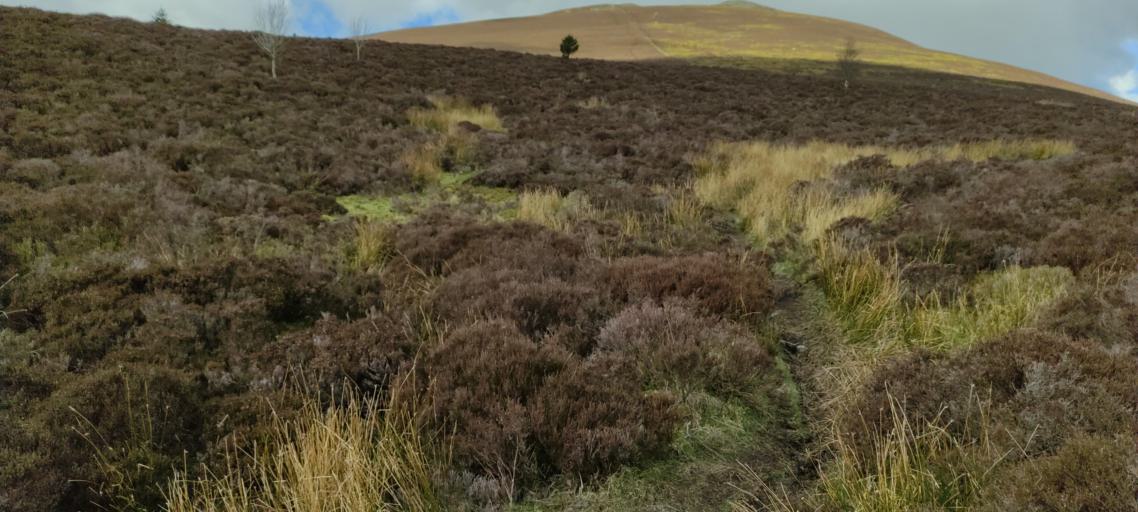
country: GB
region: England
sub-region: Cumbria
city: Keswick
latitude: 54.6685
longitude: -3.0878
